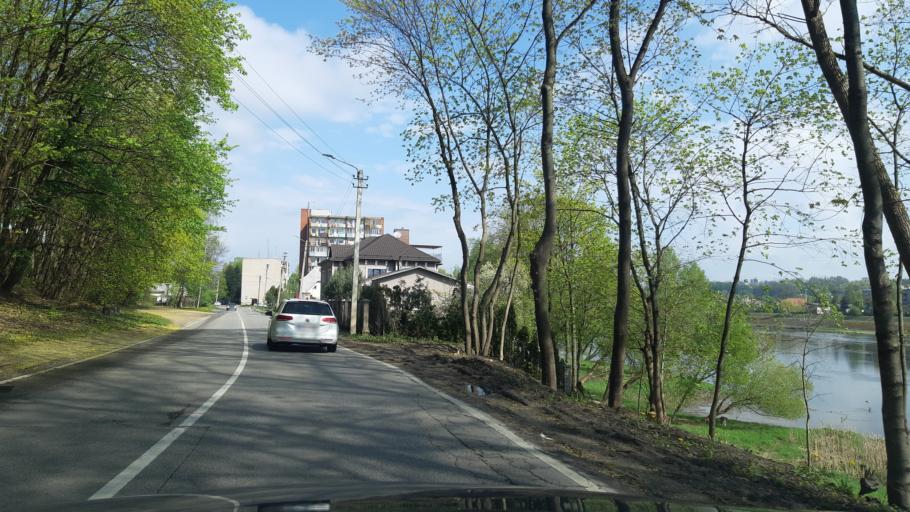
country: LT
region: Kauno apskritis
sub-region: Kaunas
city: Aleksotas
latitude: 54.8722
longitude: 23.9249
